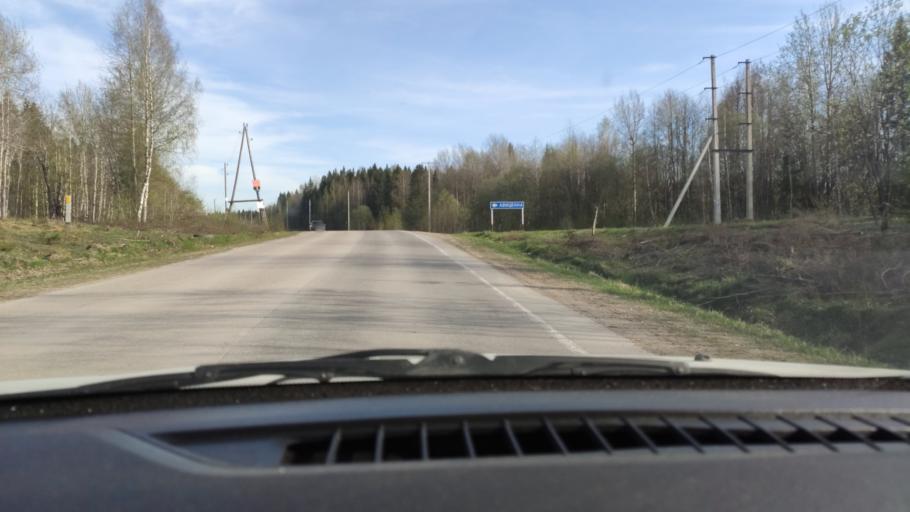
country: RU
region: Perm
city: Novyye Lyady
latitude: 57.9256
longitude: 56.6528
